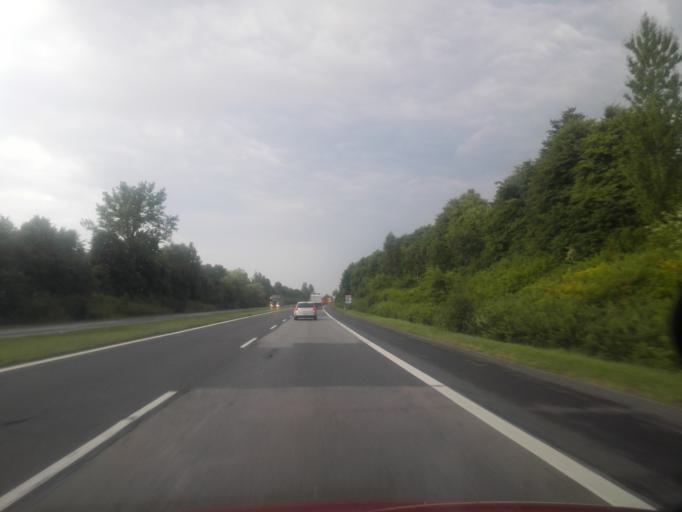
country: PL
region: Silesian Voivodeship
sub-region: Powiat czestochowski
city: Redziny
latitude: 50.8670
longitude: 19.1558
